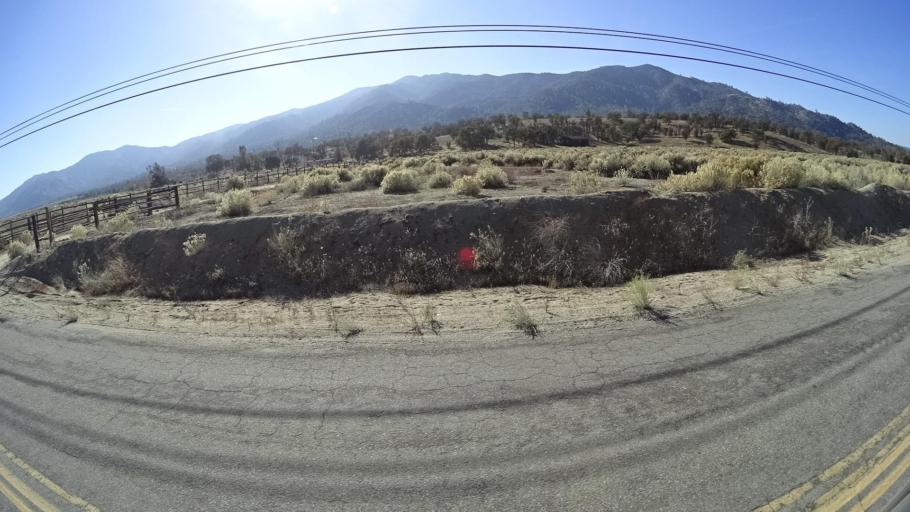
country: US
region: California
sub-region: Kern County
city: Bodfish
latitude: 35.4059
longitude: -118.5023
